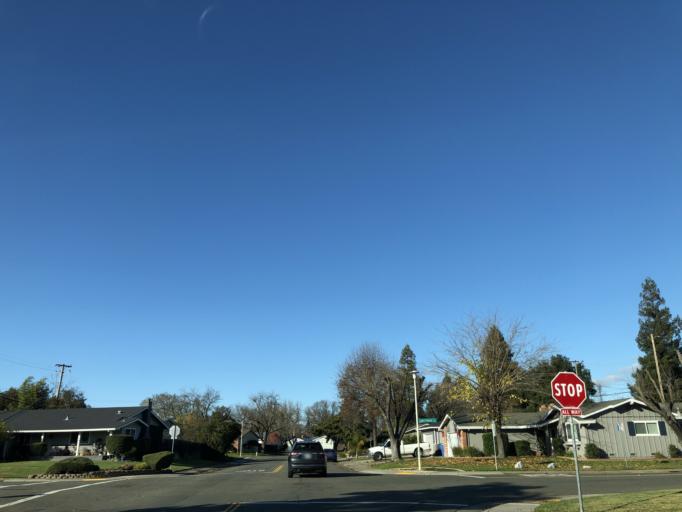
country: US
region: California
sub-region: Sacramento County
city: Rosemont
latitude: 38.5506
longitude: -121.3992
